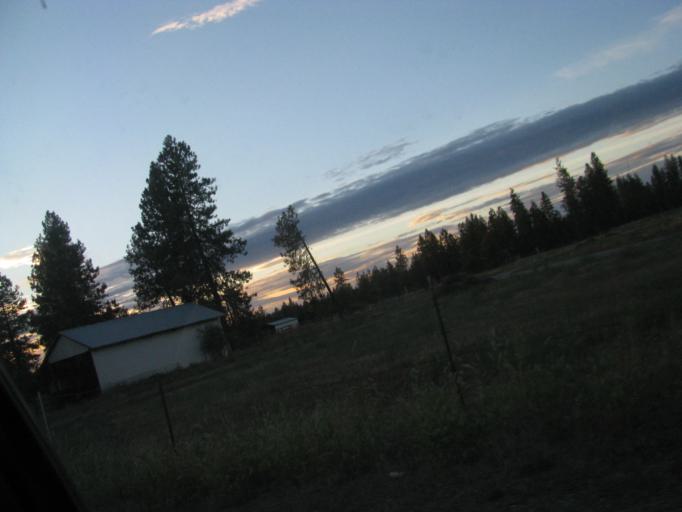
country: US
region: Washington
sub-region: Spokane County
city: Mead
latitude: 47.8964
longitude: -117.3359
